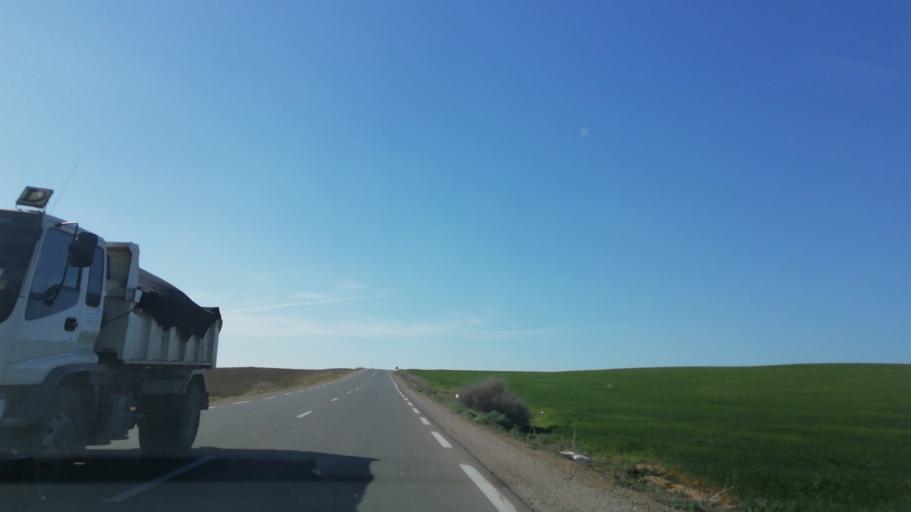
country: DZ
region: Mascara
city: Oued el Abtal
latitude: 35.4469
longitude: 0.8178
